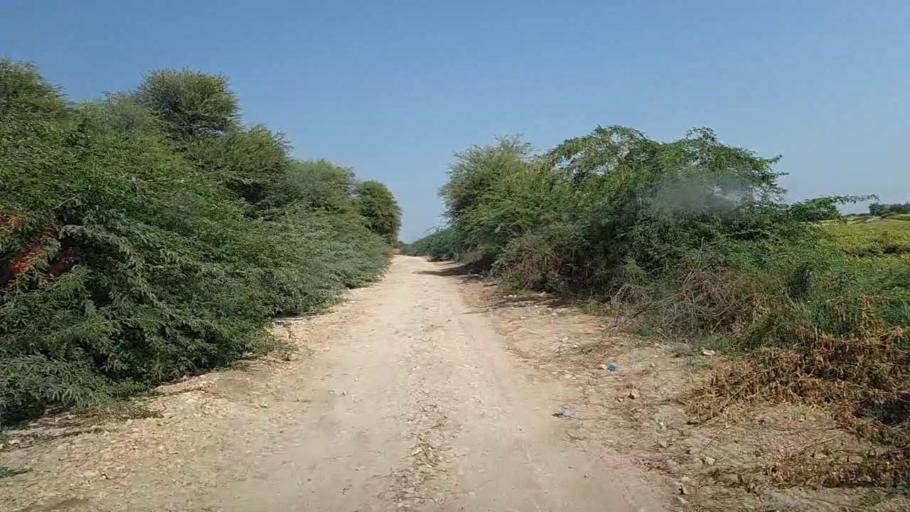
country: PK
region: Sindh
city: Mirpur Batoro
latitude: 24.7135
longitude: 68.4342
